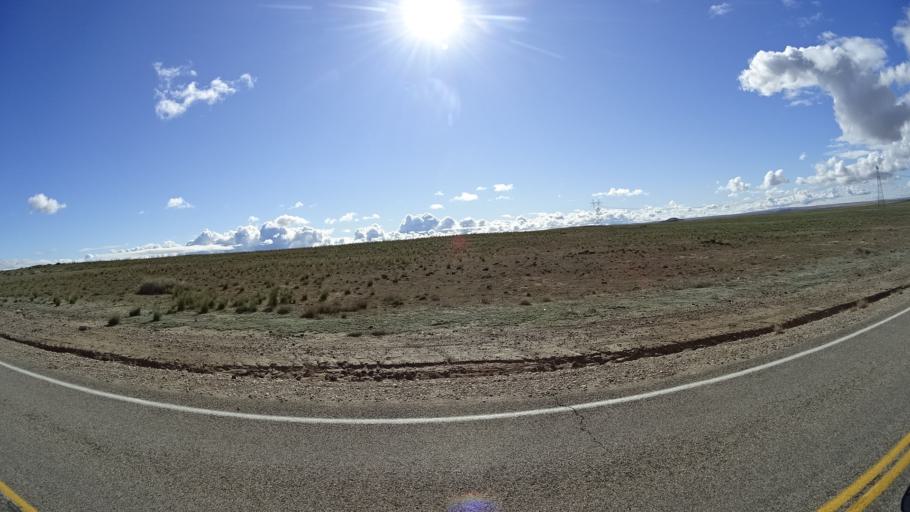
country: US
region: Idaho
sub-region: Ada County
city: Kuna
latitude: 43.3443
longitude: -116.4139
